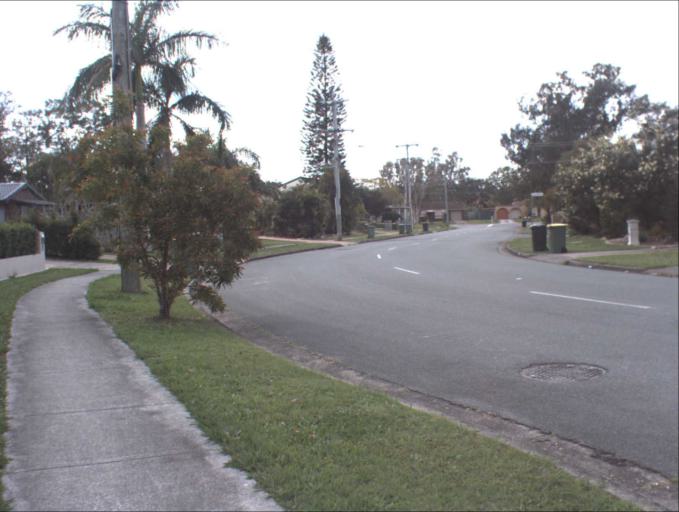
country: AU
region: Queensland
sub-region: Logan
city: Waterford West
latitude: -27.6877
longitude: 153.1542
